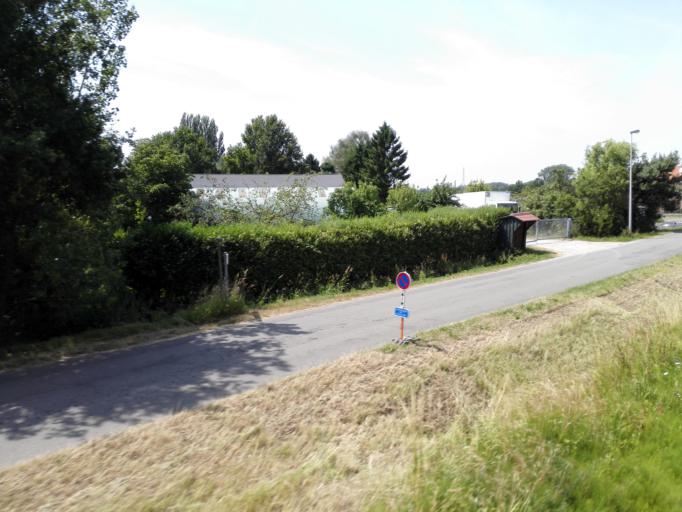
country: BE
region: Flanders
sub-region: Provincie Antwerpen
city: Boechout
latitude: 51.1479
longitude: 4.5246
